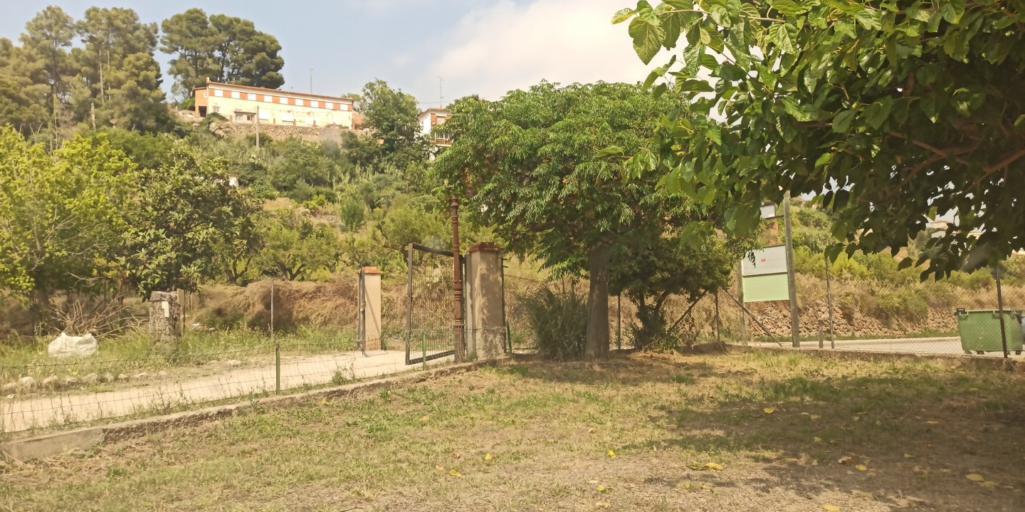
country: ES
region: Catalonia
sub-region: Provincia de Barcelona
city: Mediona
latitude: 41.4644
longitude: 1.6554
